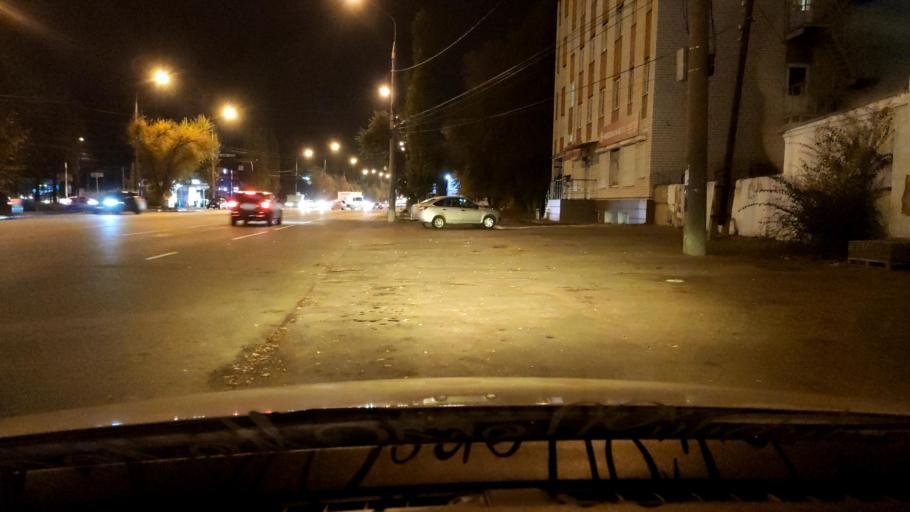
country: RU
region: Voronezj
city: Voronezh
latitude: 51.6805
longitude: 39.1665
